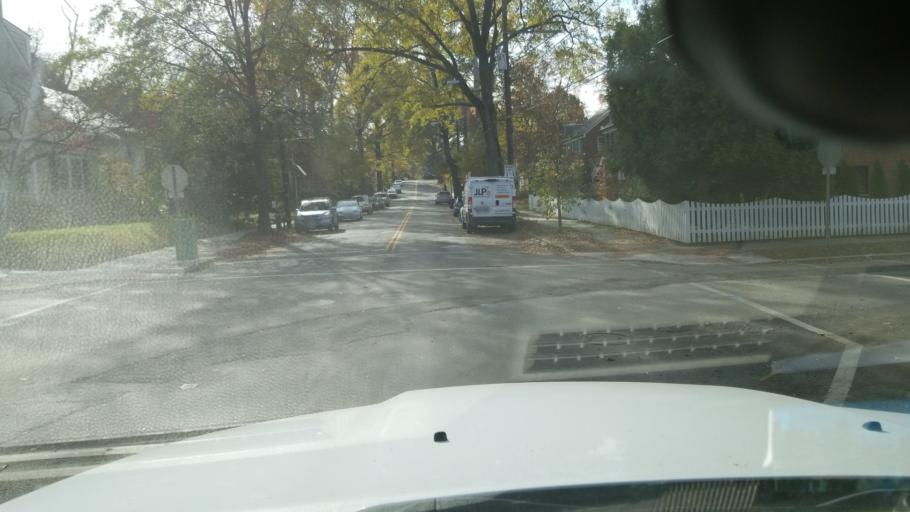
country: US
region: Maryland
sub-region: Montgomery County
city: Friendship Village
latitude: 38.9498
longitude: -77.0906
